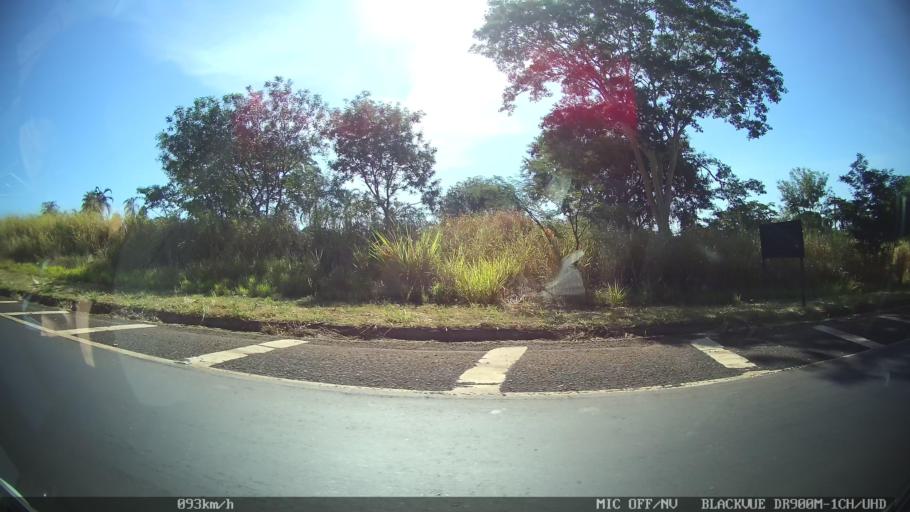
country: BR
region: Sao Paulo
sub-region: Barretos
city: Barretos
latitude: -20.6079
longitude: -48.7456
